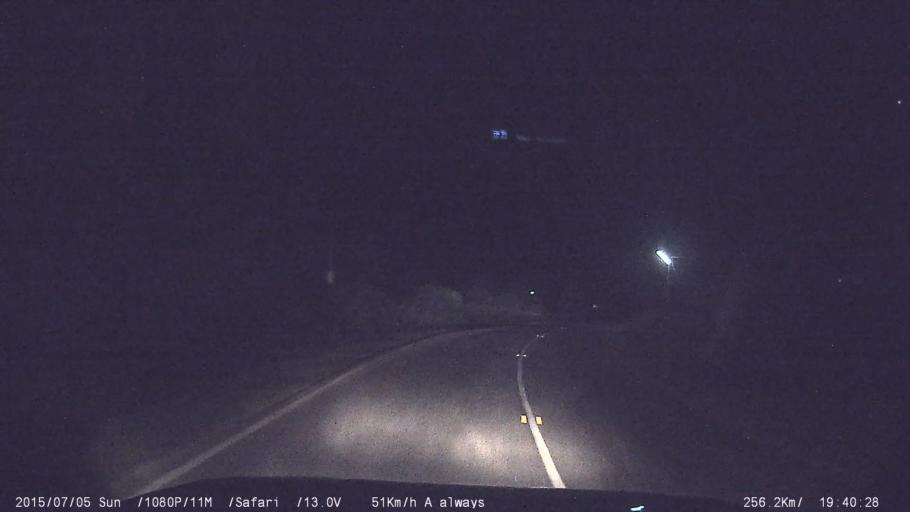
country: IN
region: Kerala
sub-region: Palakkad district
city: Palakkad
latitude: 10.7520
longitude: 76.5599
